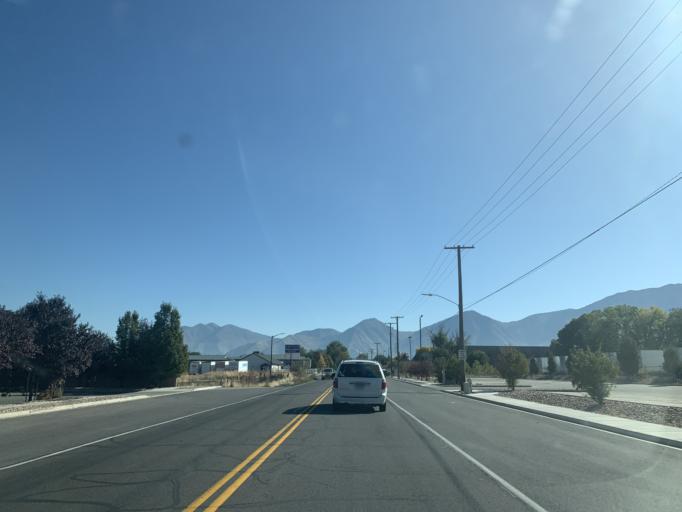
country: US
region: Utah
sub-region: Utah County
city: Payson
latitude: 40.0436
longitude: -111.7518
